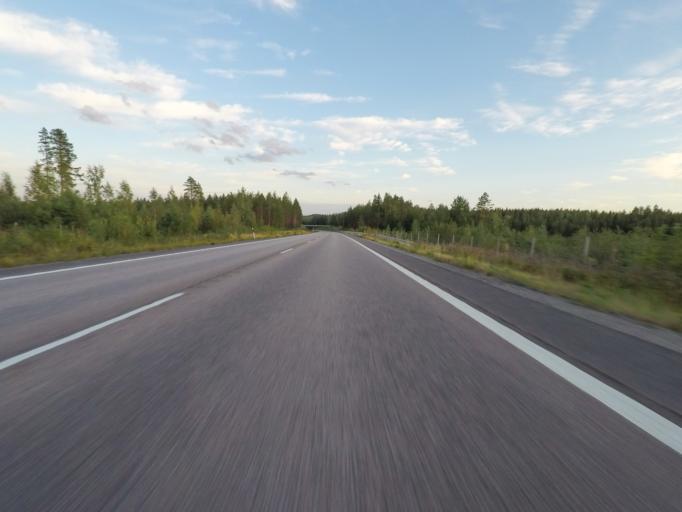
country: FI
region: Central Finland
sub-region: Jyvaeskylae
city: Saeynaetsalo
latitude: 62.2038
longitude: 25.8905
